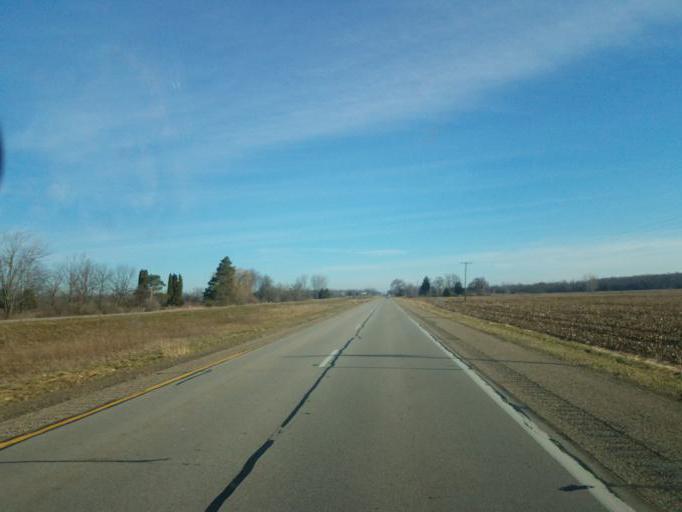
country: US
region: Michigan
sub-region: Clinton County
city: Saint Johns
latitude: 43.1217
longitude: -84.5631
